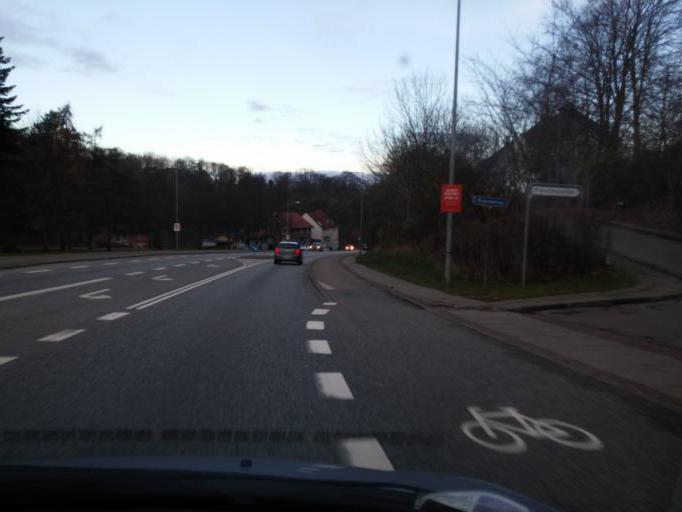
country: DK
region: South Denmark
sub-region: Vejle Kommune
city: Vejle
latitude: 55.6978
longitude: 9.5377
